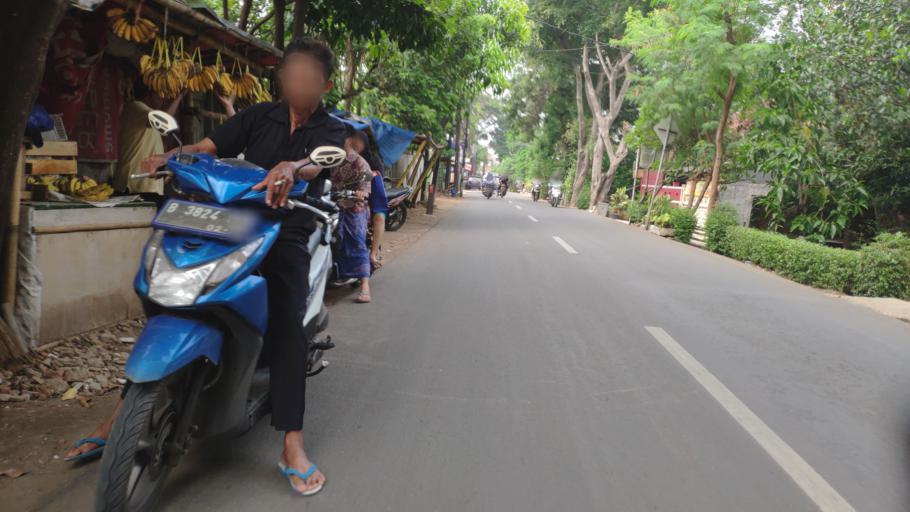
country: ID
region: West Java
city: Depok
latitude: -6.3458
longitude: 106.8116
